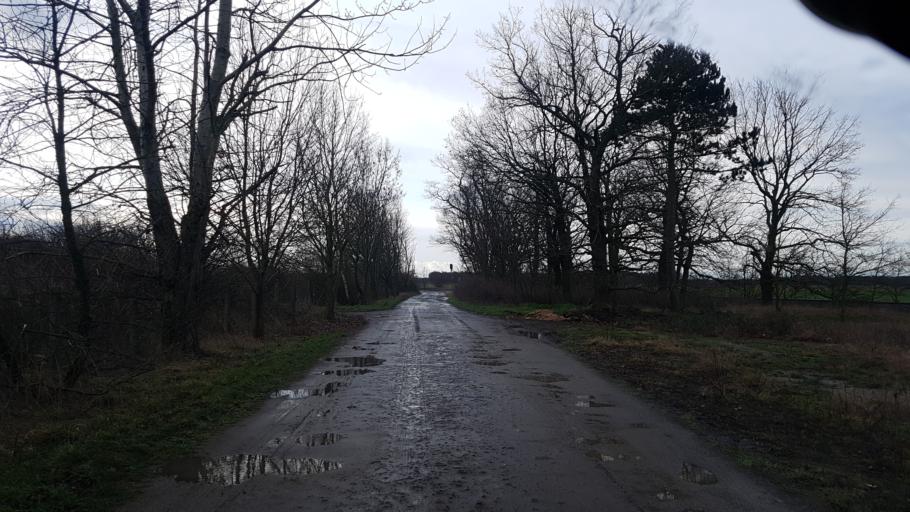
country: DE
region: Brandenburg
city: Herzberg
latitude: 51.6767
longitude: 13.2390
